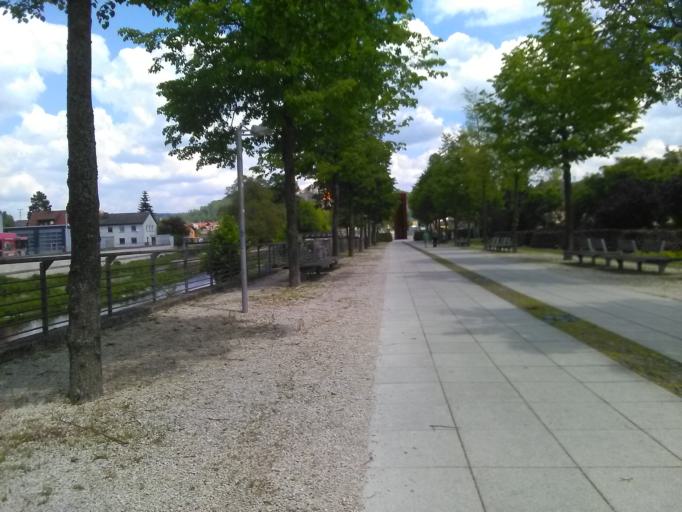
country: DE
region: Bavaria
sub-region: Upper Franconia
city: Kronach
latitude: 50.2363
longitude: 11.3203
